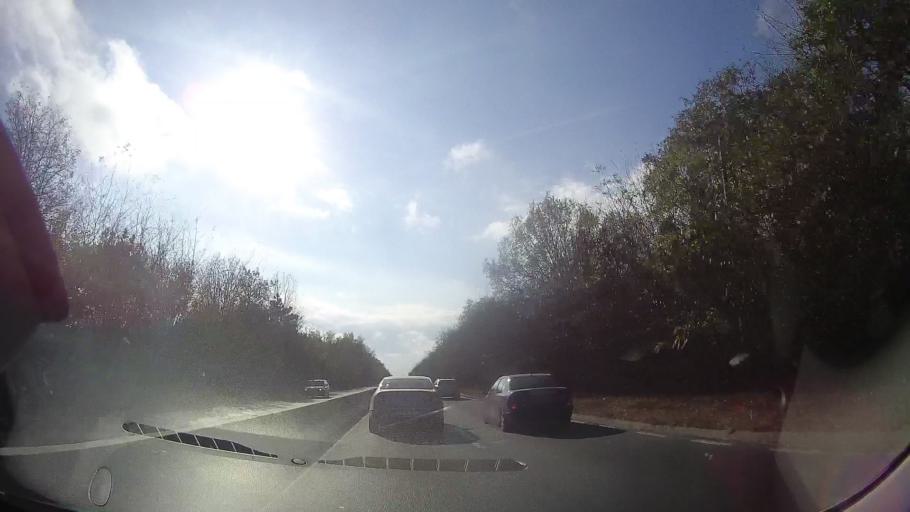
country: RO
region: Constanta
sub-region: Comuna Agigea
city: Agigea
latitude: 44.1289
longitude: 28.6163
